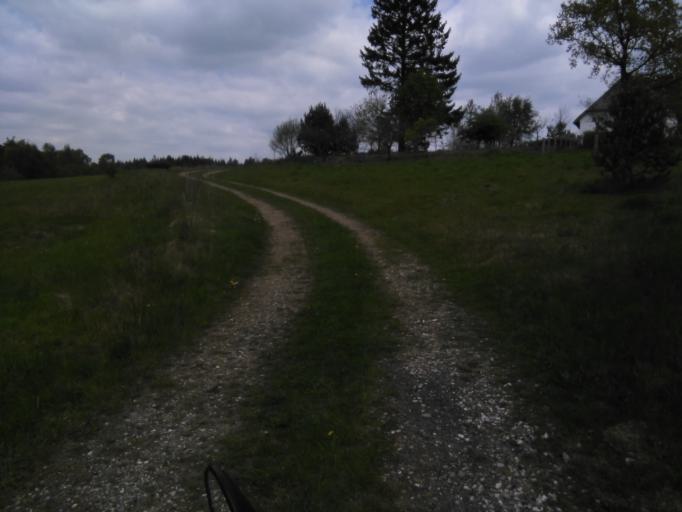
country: DK
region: Central Jutland
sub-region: Silkeborg Kommune
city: Svejbaek
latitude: 56.0539
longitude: 9.6351
